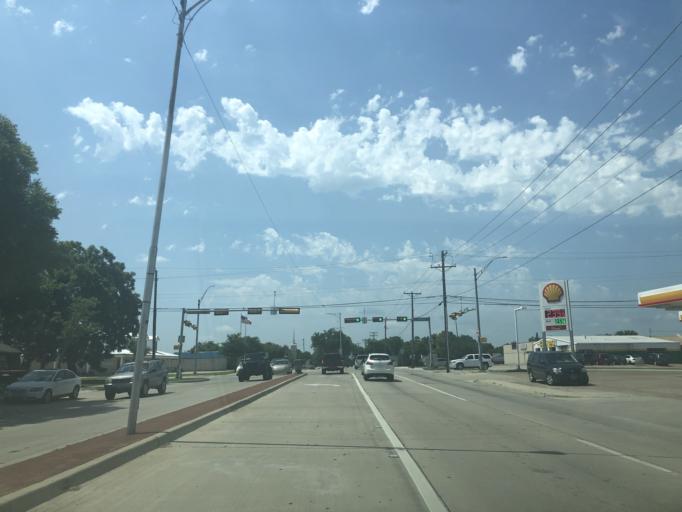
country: US
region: Texas
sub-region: Dallas County
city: Grand Prairie
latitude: 32.7210
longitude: -97.0149
